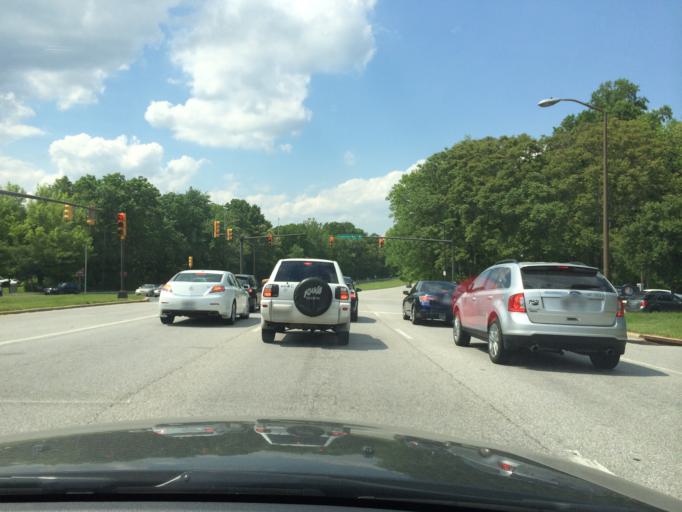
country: US
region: Maryland
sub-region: Howard County
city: Riverside
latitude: 39.1850
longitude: -76.8502
